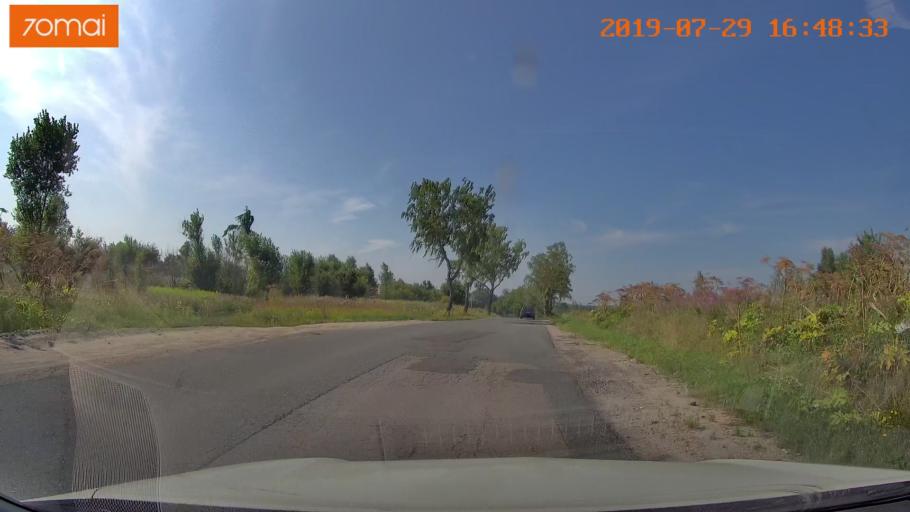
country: RU
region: Kaliningrad
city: Primorsk
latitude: 54.7875
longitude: 20.0758
